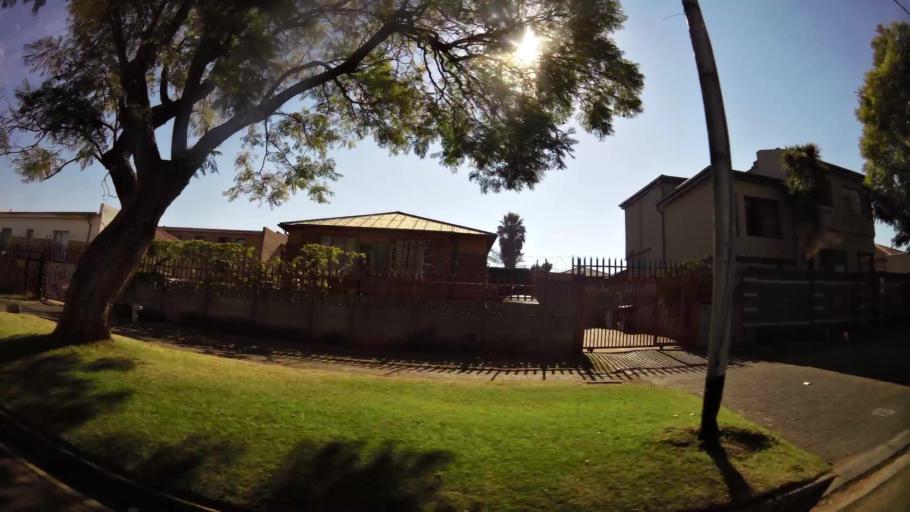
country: ZA
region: Gauteng
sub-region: City of Johannesburg Metropolitan Municipality
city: Johannesburg
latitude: -26.1987
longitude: 27.9884
